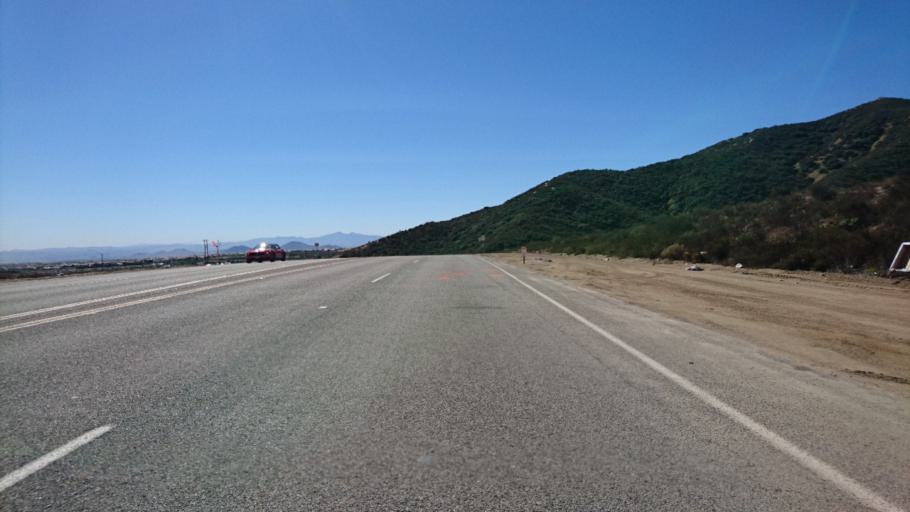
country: US
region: California
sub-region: San Bernardino County
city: Muscoy
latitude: 34.2009
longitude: -117.4187
